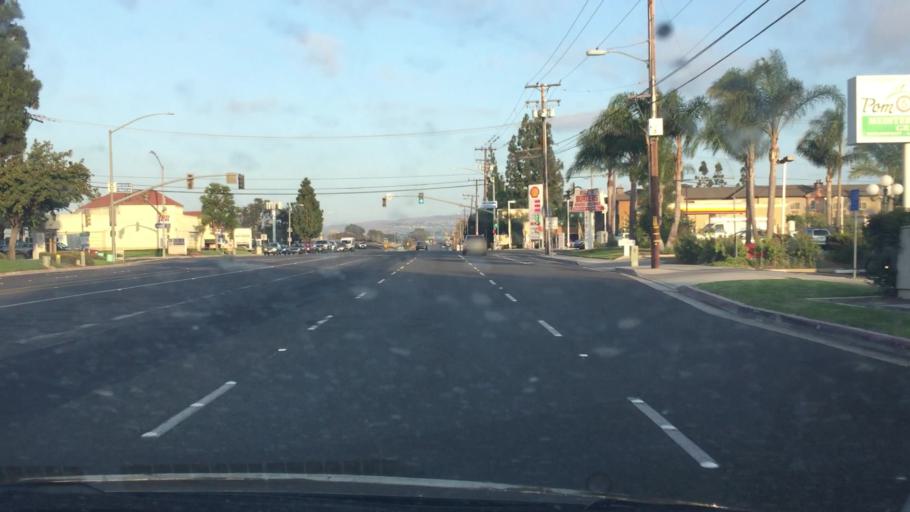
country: US
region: California
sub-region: Orange County
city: Costa Mesa
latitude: 33.6671
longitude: -117.8828
